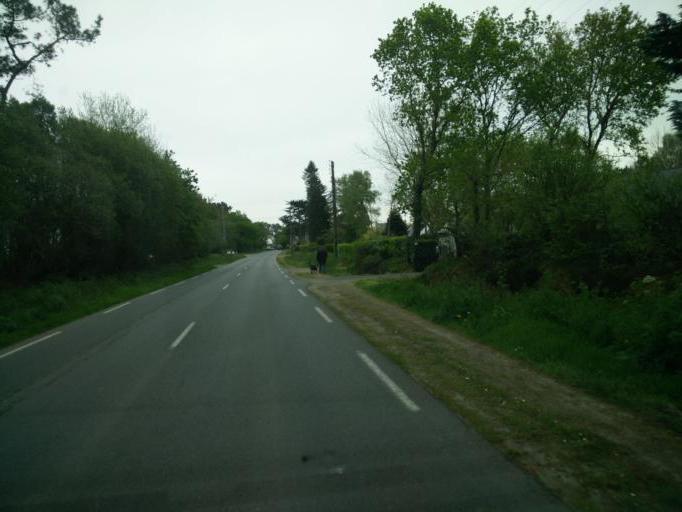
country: FR
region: Brittany
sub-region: Departement des Cotes-d'Armor
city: Trebeurden
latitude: 48.7616
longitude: -3.5418
